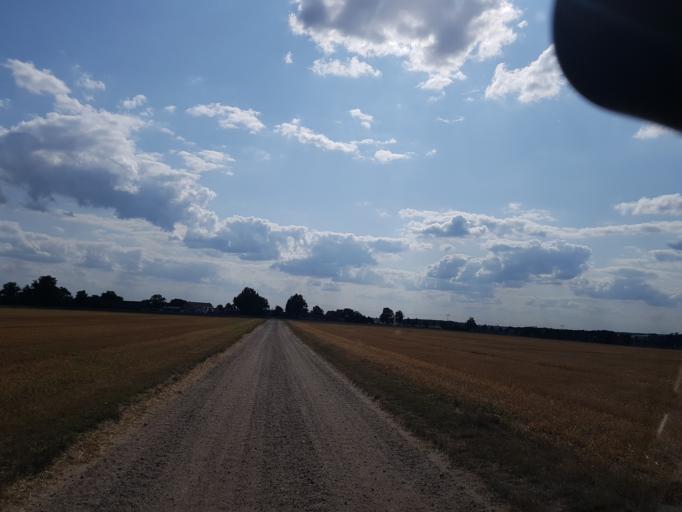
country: DE
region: Brandenburg
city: Finsterwalde
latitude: 51.6344
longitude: 13.7688
